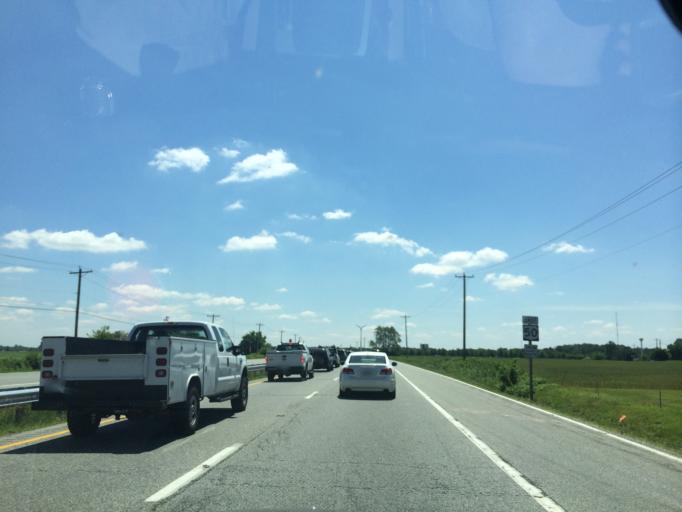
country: US
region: Maryland
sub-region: Queen Anne's County
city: Centreville
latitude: 38.9590
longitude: -76.0933
